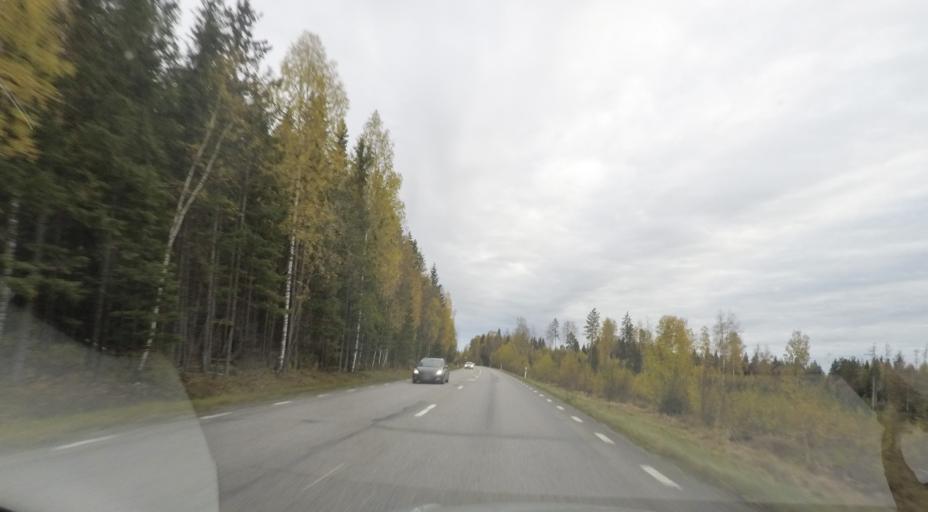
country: SE
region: OErebro
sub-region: Hallefors Kommun
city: Haellefors
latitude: 59.7191
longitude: 14.5260
